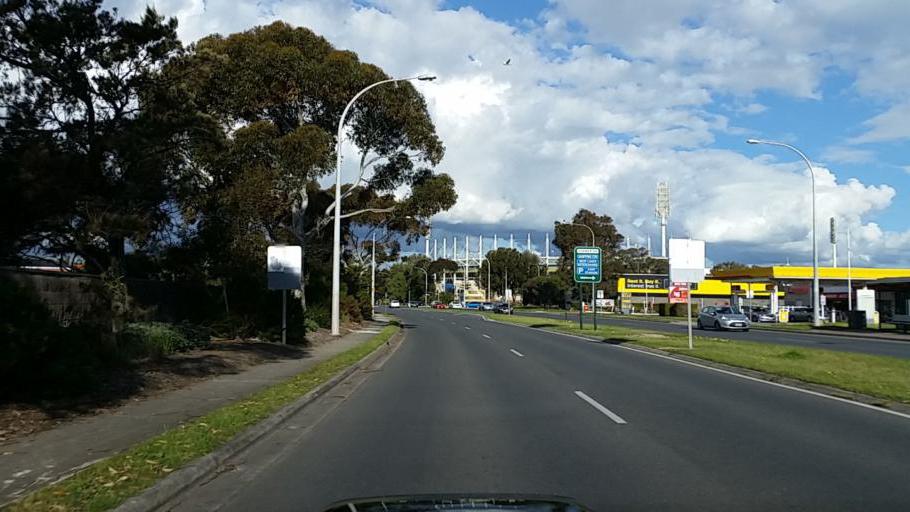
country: AU
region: South Australia
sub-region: Charles Sturt
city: West Lakes Shore
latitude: -34.8763
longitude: 138.4924
